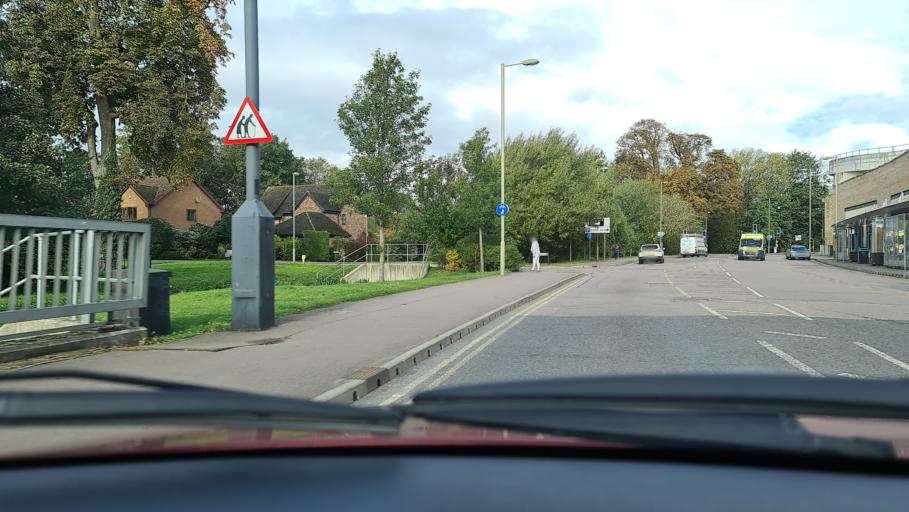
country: GB
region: England
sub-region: Oxfordshire
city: Bicester
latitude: 51.8981
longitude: -1.1536
